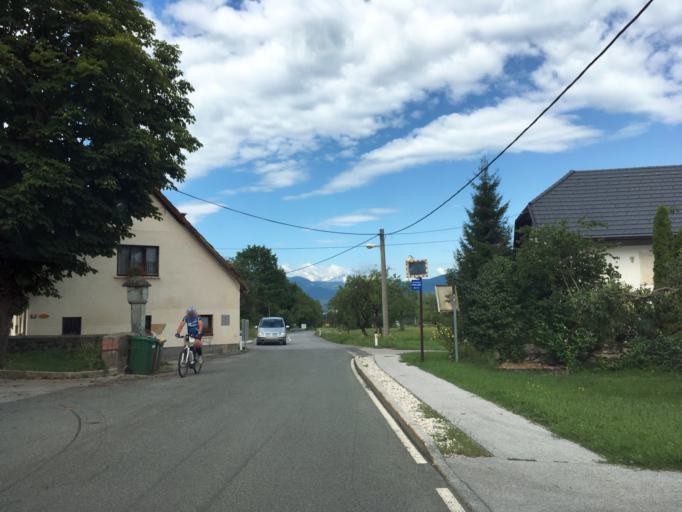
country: SI
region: Radovljica
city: Radovljica
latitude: 46.3756
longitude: 14.1902
